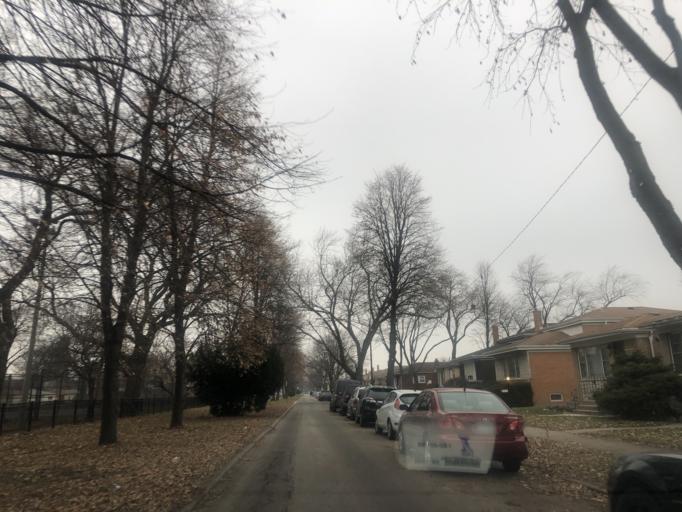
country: US
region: Illinois
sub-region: Cook County
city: Evergreen Park
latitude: 41.7446
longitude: -87.6291
